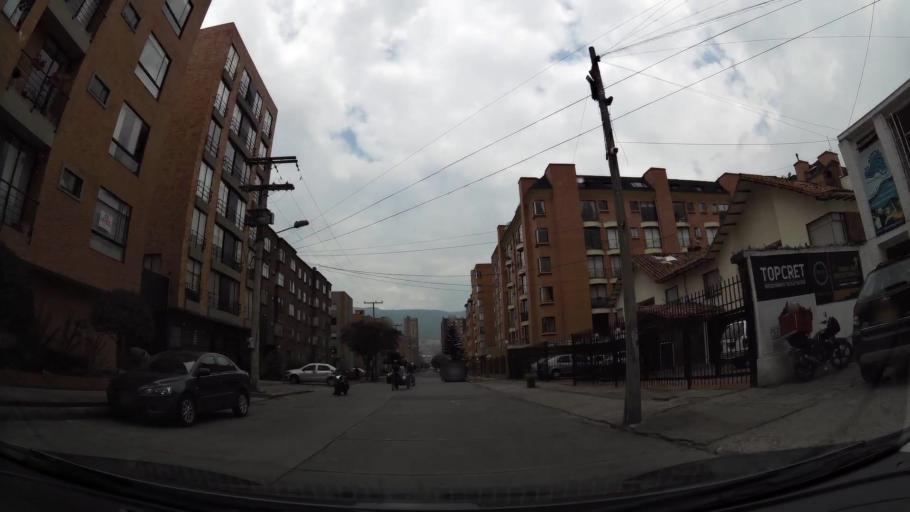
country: CO
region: Bogota D.C.
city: Barrio San Luis
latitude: 4.7270
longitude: -74.0403
